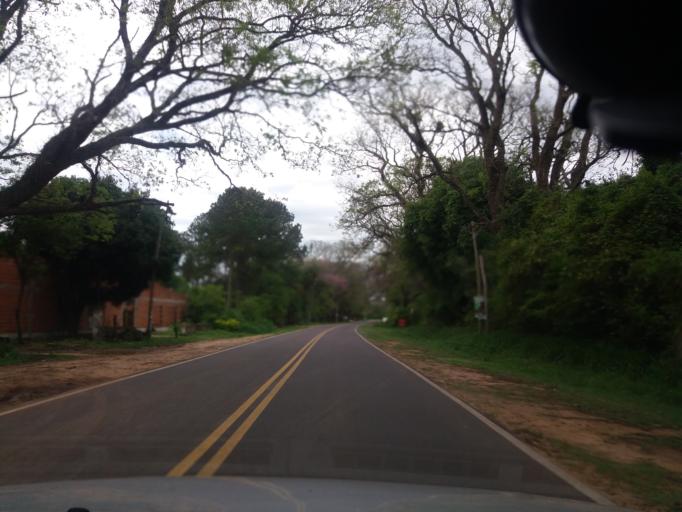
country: AR
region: Corrientes
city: Riachuelo
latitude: -27.4568
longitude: -58.6829
